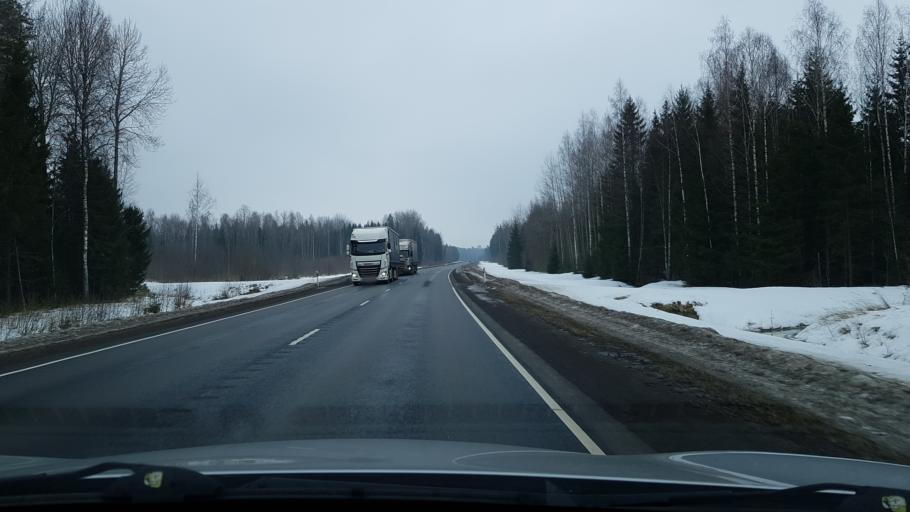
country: EE
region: Valgamaa
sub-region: Valga linn
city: Valga
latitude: 57.8700
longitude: 26.1500
